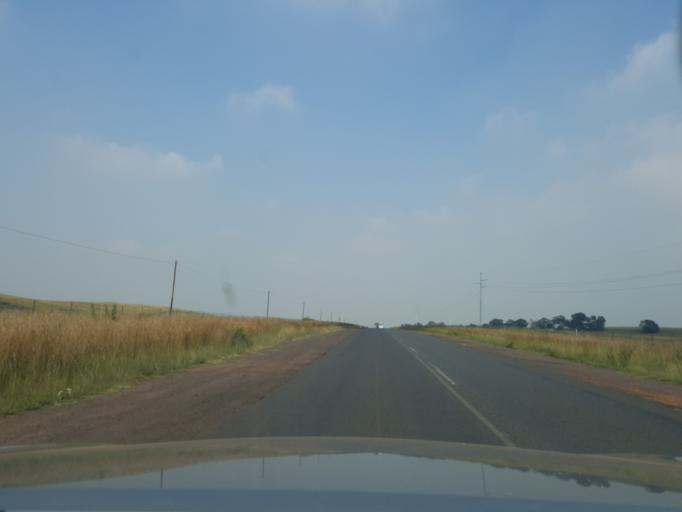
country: ZA
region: Mpumalanga
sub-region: Nkangala District Municipality
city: Witbank
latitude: -26.0146
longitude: 29.3287
